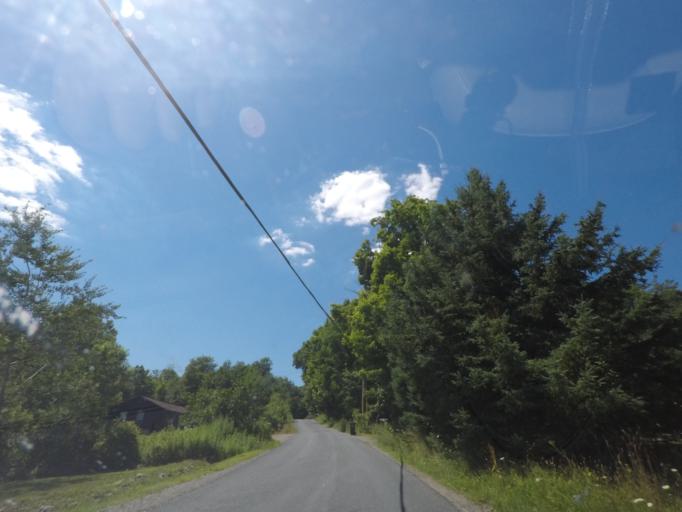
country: US
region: New York
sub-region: Rensselaer County
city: Averill Park
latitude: 42.5745
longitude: -73.5153
